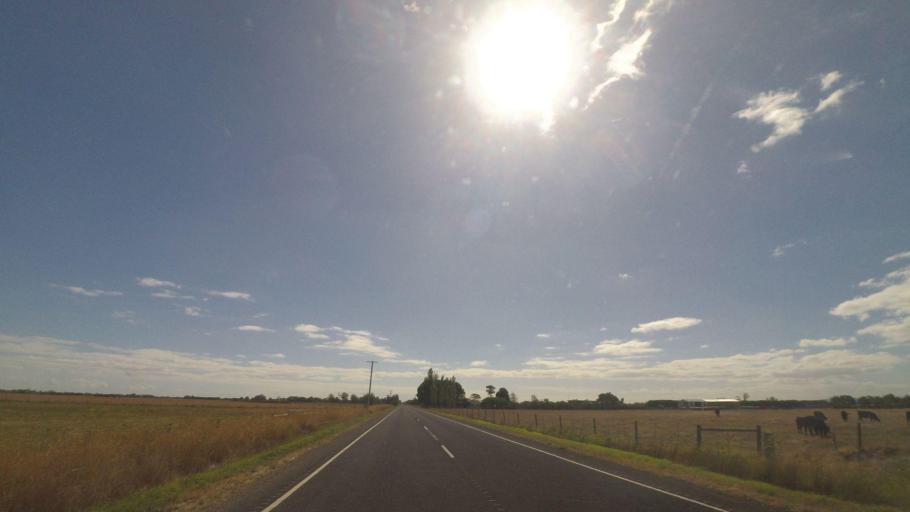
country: AU
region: Victoria
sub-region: Cardinia
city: Pakenham South
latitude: -38.1590
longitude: 145.5253
